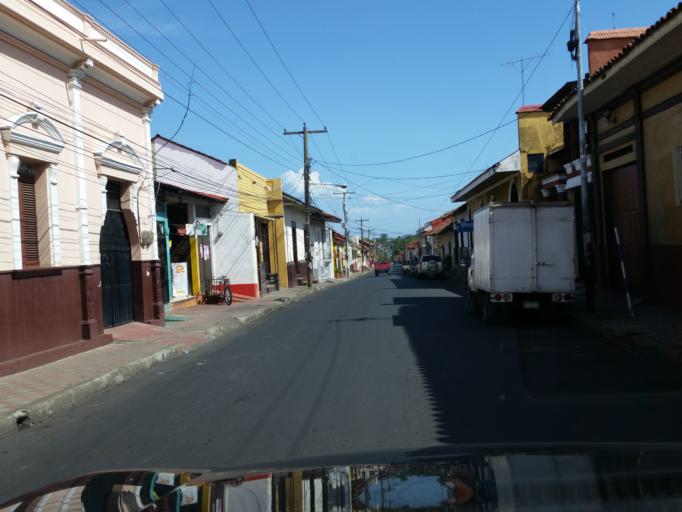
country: NI
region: Leon
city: Leon
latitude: 12.4376
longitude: -86.8747
